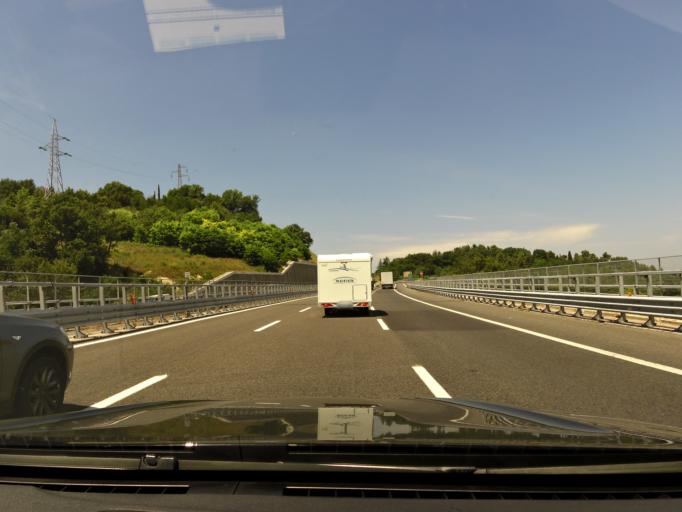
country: IT
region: The Marches
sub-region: Provincia di Pesaro e Urbino
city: Pesaro
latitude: 43.8667
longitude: 12.9268
